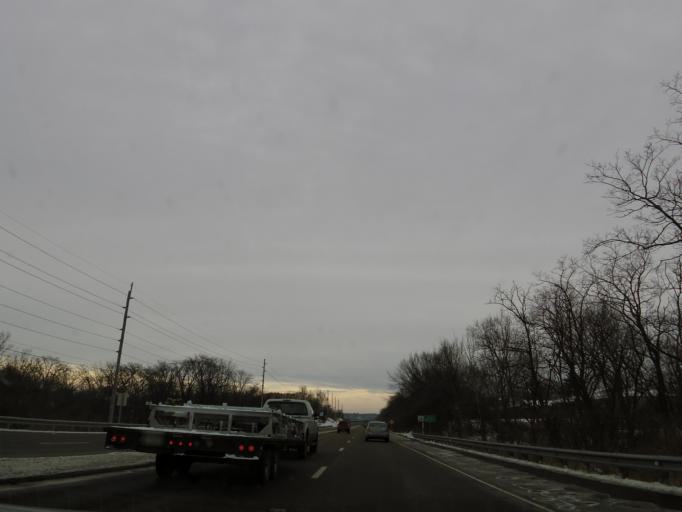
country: US
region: Illinois
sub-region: LaSalle County
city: Peru
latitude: 41.3352
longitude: -89.1201
